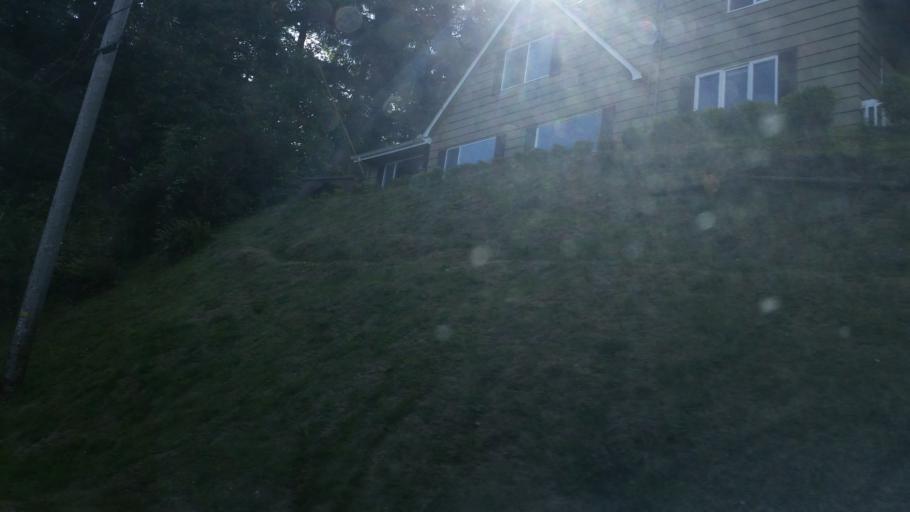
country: US
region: Oregon
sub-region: Clatsop County
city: Astoria
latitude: 46.1879
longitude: -123.8086
